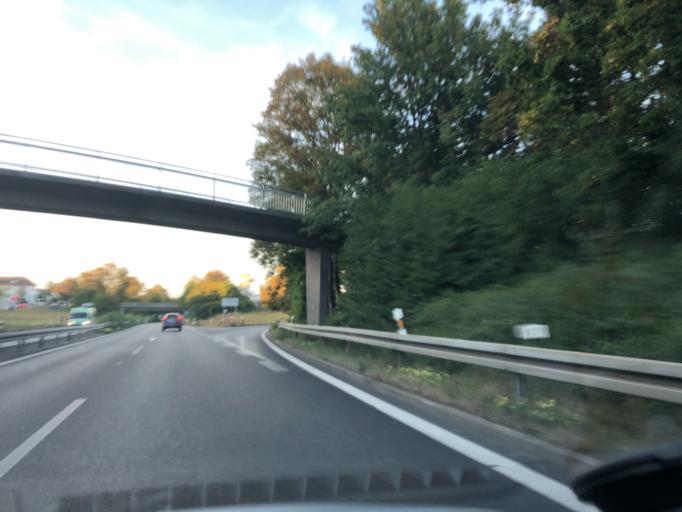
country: DE
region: Baden-Wuerttemberg
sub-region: Regierungsbezirk Stuttgart
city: Kornwestheim
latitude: 48.8584
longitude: 9.1962
